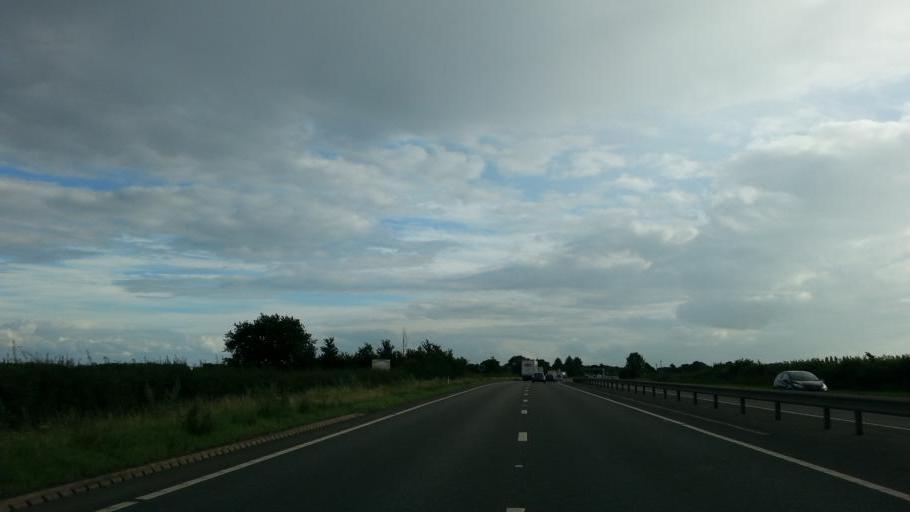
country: GB
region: England
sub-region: Nottinghamshire
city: South Collingham
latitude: 53.1352
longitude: -0.8084
